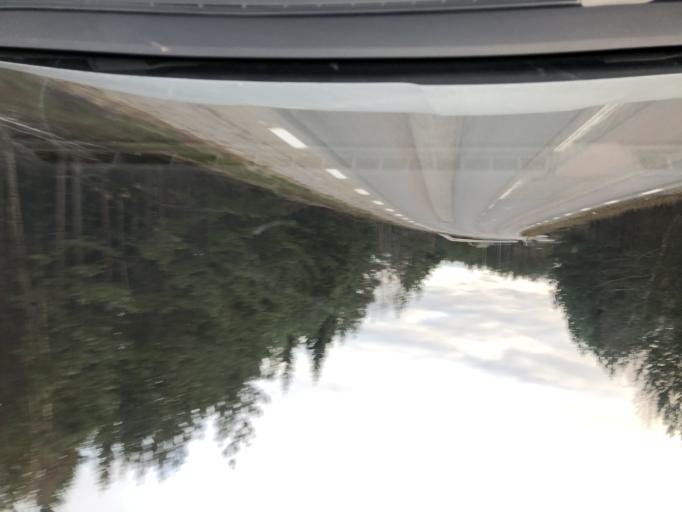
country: SE
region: Gaevleborg
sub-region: Hudiksvalls Kommun
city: Iggesund
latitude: 61.5521
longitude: 16.9806
